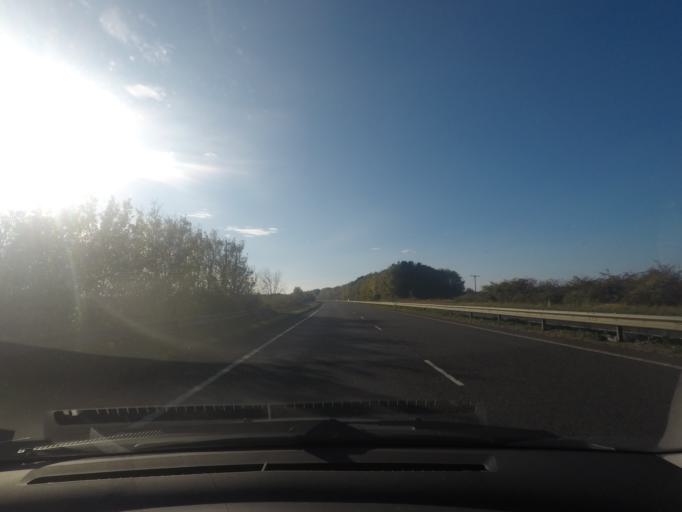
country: GB
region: England
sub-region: North Lincolnshire
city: Barton upon Humber
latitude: 53.6541
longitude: -0.4510
